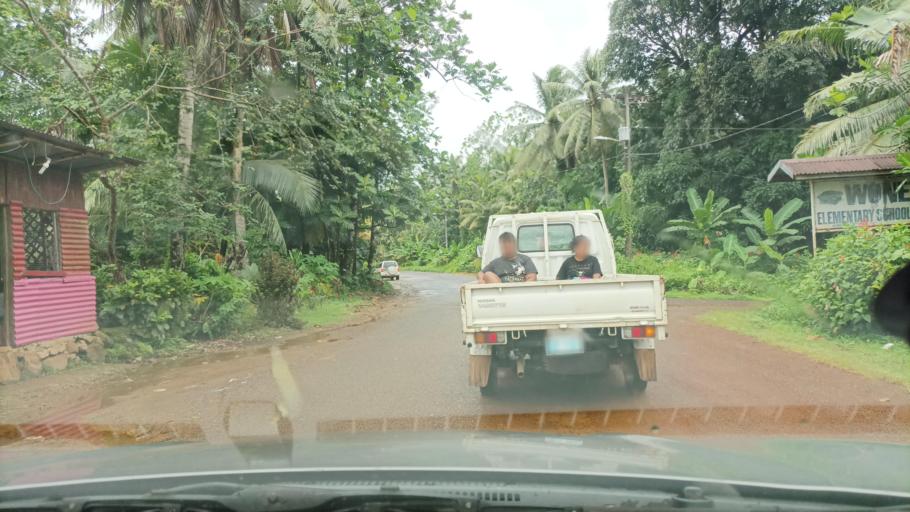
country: FM
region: Pohnpei
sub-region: Madolenihm Municipality
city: Madolenihm Municipality Government
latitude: 6.8133
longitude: 158.2409
